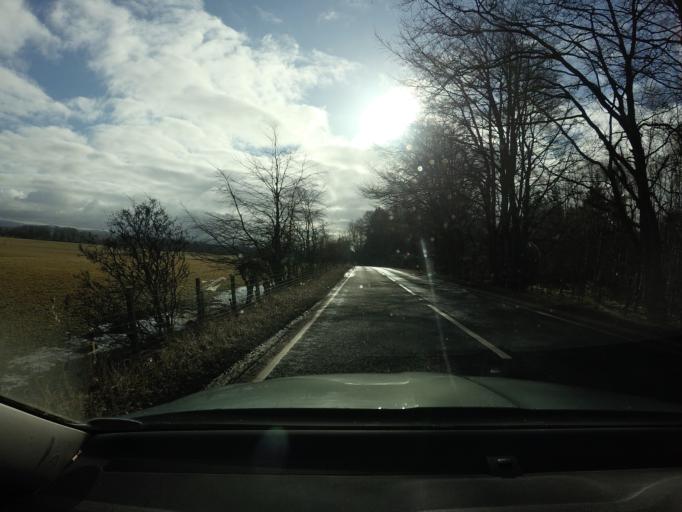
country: GB
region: Scotland
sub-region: South Lanarkshire
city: Forth
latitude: 55.7034
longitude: -3.7185
